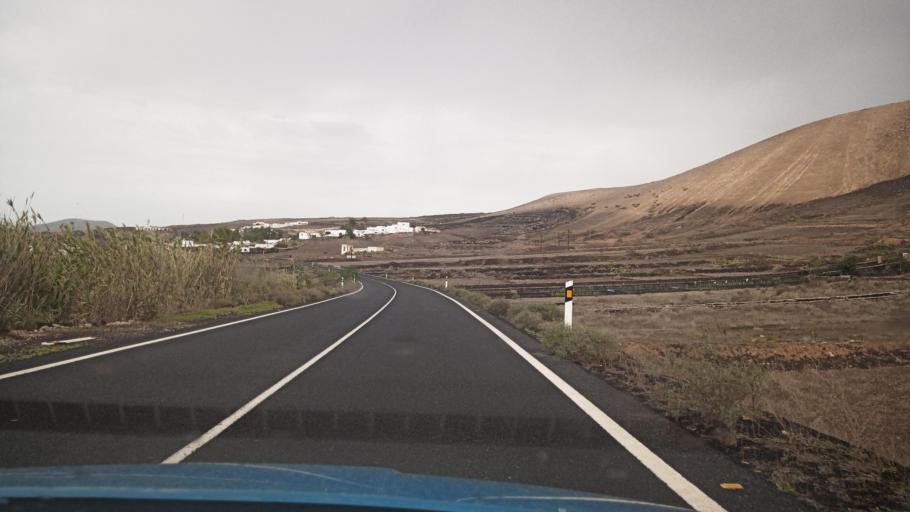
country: ES
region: Canary Islands
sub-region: Provincia de Las Palmas
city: Yaiza
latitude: 28.9431
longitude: -13.7403
